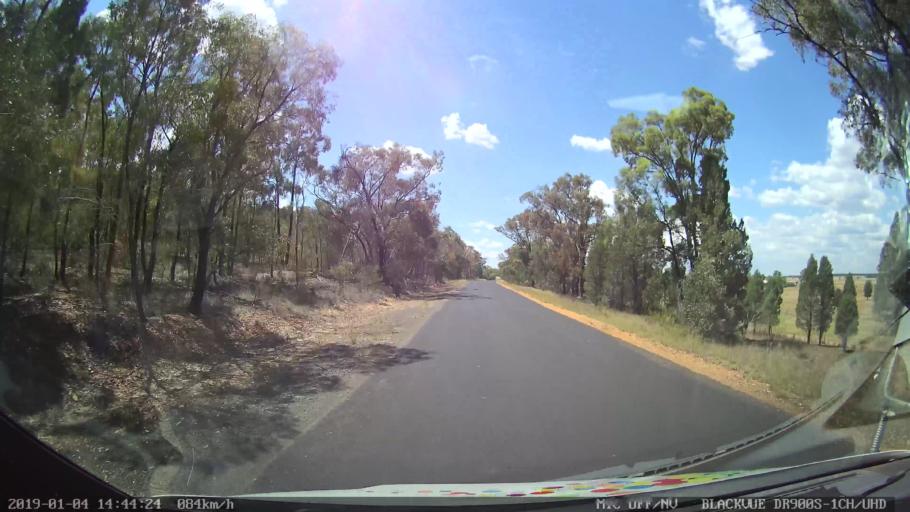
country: AU
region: New South Wales
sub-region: Dubbo Municipality
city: Dubbo
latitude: -32.1068
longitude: 148.6556
